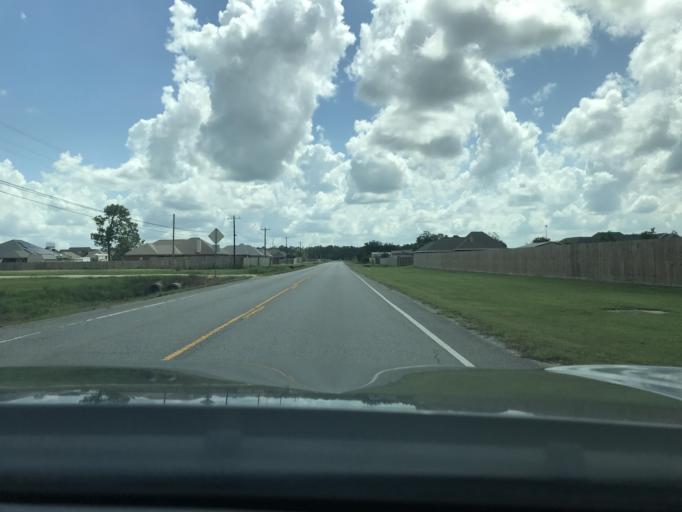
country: US
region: Louisiana
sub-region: Calcasieu Parish
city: Moss Bluff
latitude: 30.3408
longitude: -93.2425
